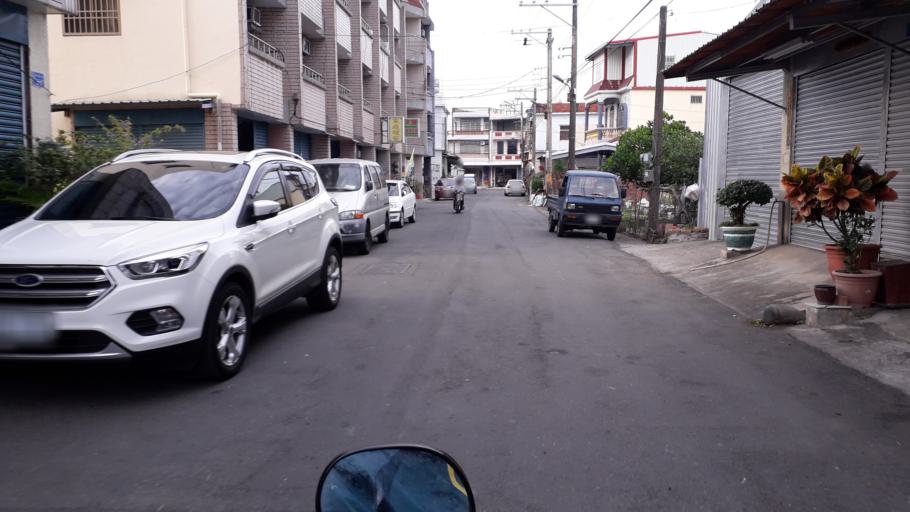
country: TW
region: Taiwan
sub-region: Pingtung
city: Pingtung
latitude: 22.3648
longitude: 120.6016
